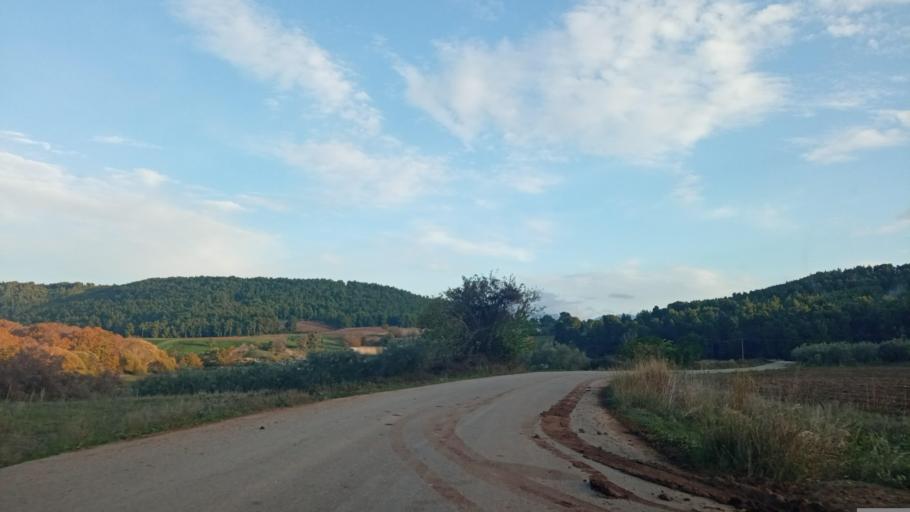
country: GR
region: Central Greece
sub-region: Nomos Evvoias
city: Kastella
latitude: 38.5508
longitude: 23.7168
